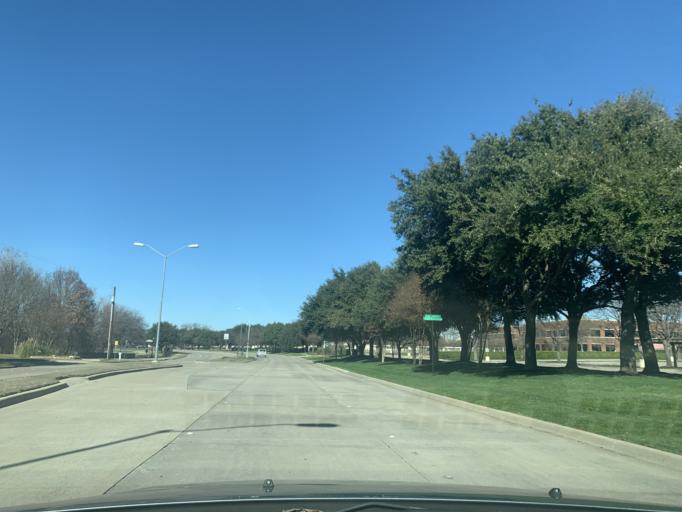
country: US
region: Texas
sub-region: Denton County
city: The Colony
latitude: 33.0500
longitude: -96.8330
